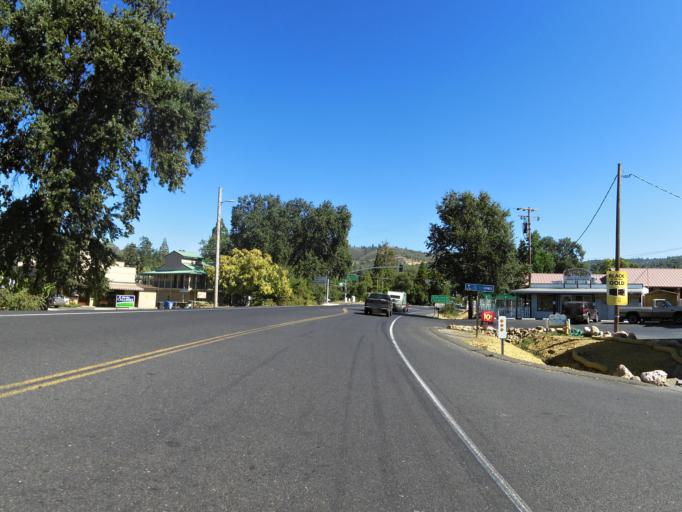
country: US
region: California
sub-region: Calaveras County
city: Murphys
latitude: 38.1382
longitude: -120.4566
